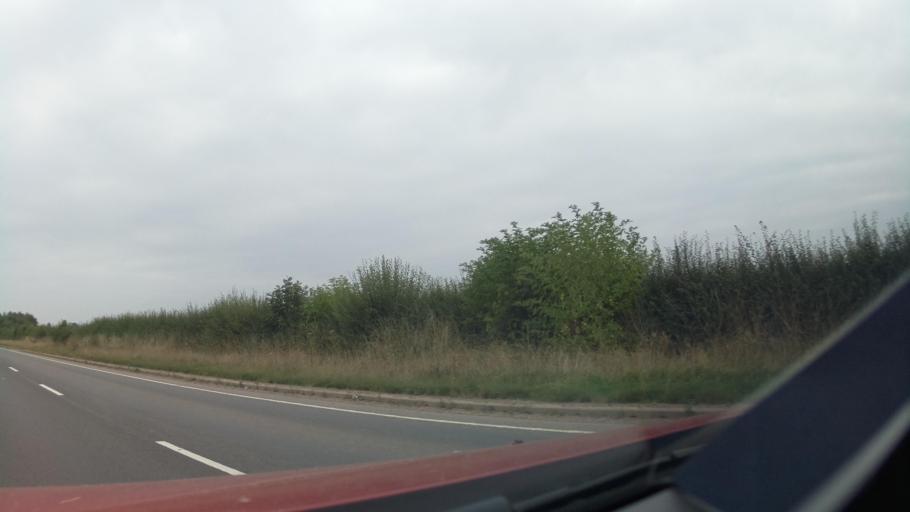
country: GB
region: England
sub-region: Shropshire
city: Stoke upon Tern
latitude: 52.8765
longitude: -2.5527
